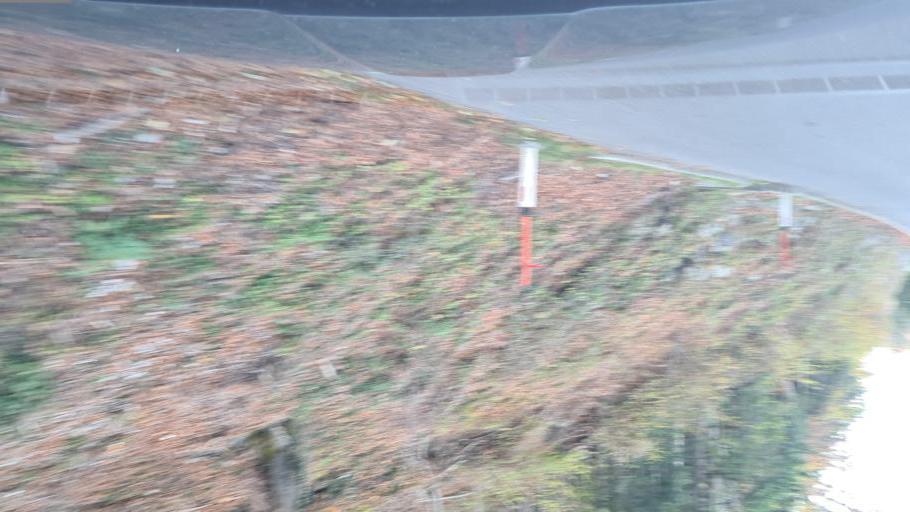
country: AT
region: Salzburg
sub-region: Politischer Bezirk Hallein
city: Golling an der Salzach
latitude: 47.6214
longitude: 13.1856
